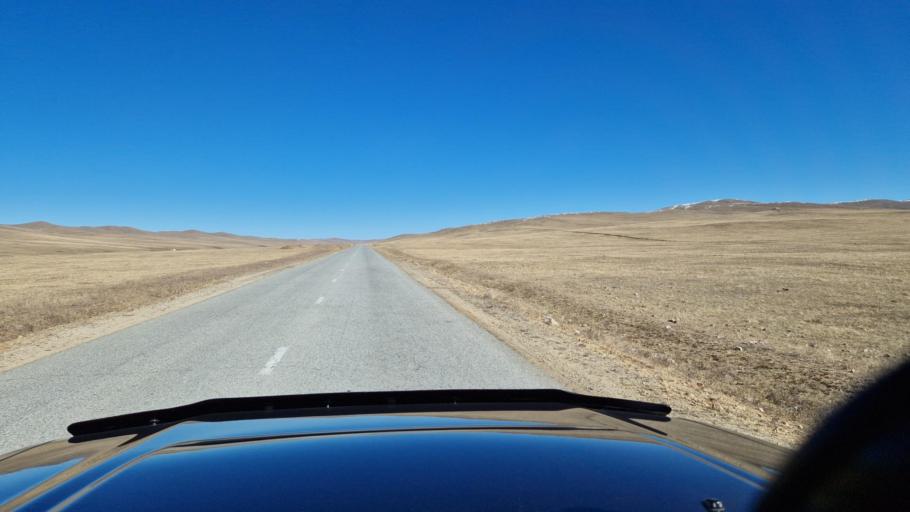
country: MN
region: Hentiy
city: Modot
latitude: 47.7377
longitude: 108.6018
